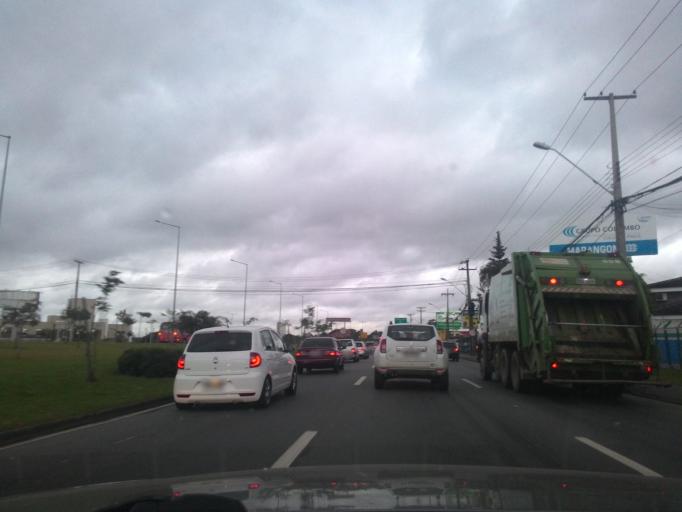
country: BR
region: Parana
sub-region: Curitiba
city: Curitiba
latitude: -25.4730
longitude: -49.2566
